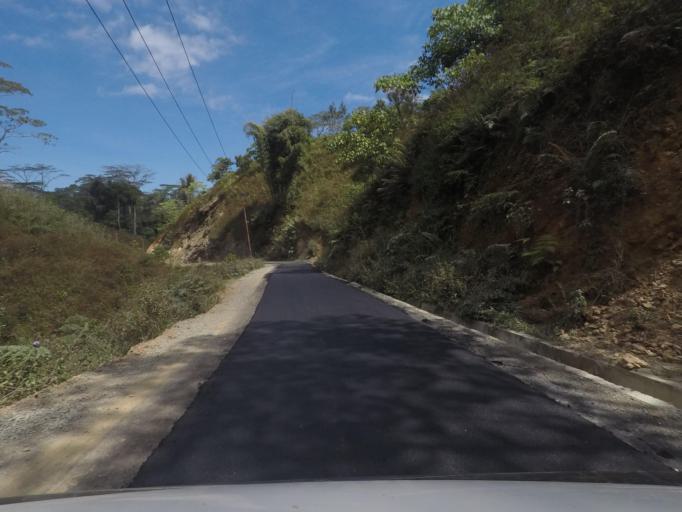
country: TL
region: Ermera
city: Gleno
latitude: -8.7516
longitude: 125.3391
